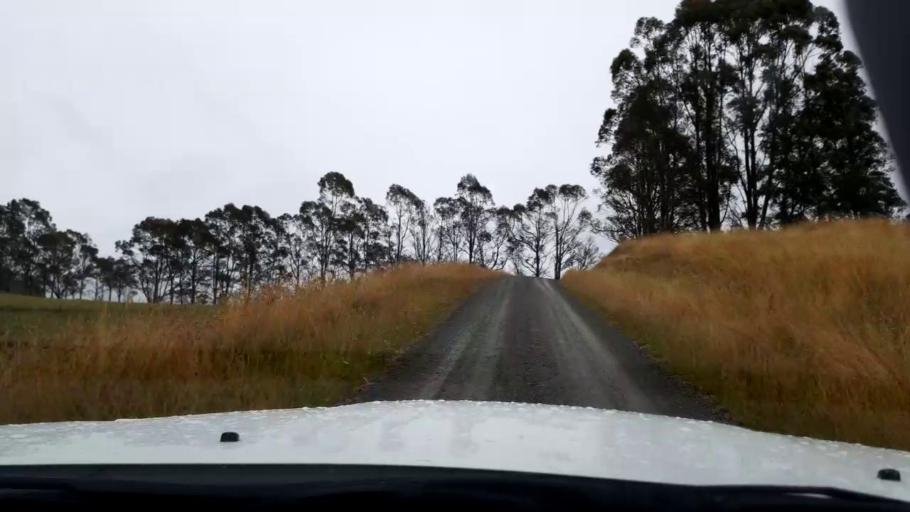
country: NZ
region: Canterbury
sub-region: Timaru District
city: Pleasant Point
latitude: -44.1729
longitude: 171.1049
